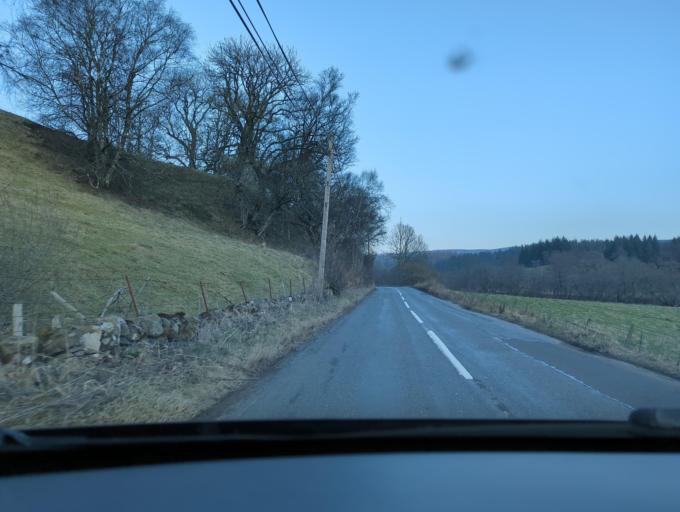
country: GB
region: Scotland
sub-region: Perth and Kinross
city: Methven
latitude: 56.5378
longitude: -3.6880
